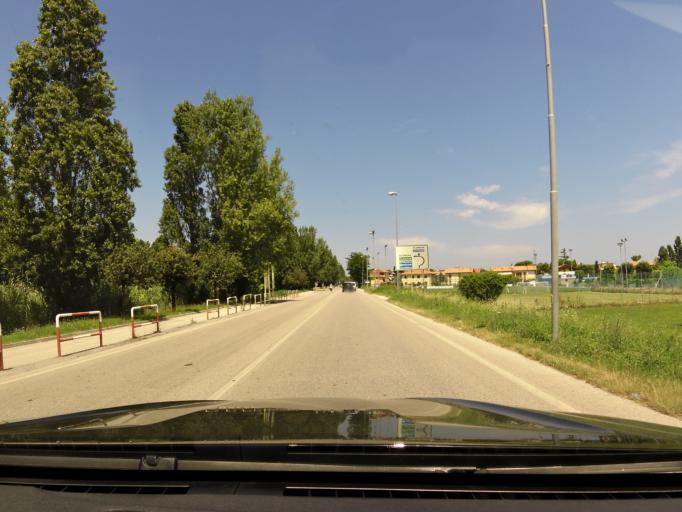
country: IT
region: The Marches
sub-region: Provincia di Pesaro e Urbino
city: Fano
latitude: 43.8294
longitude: 13.0150
